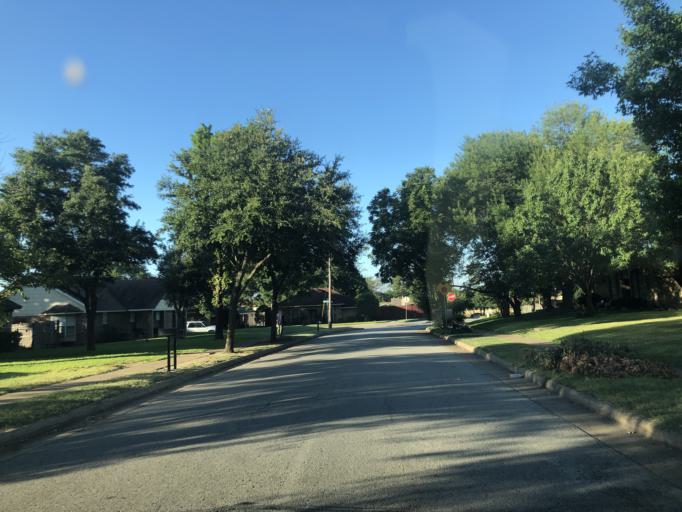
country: US
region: Texas
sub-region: Dallas County
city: Duncanville
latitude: 32.6459
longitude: -96.9471
